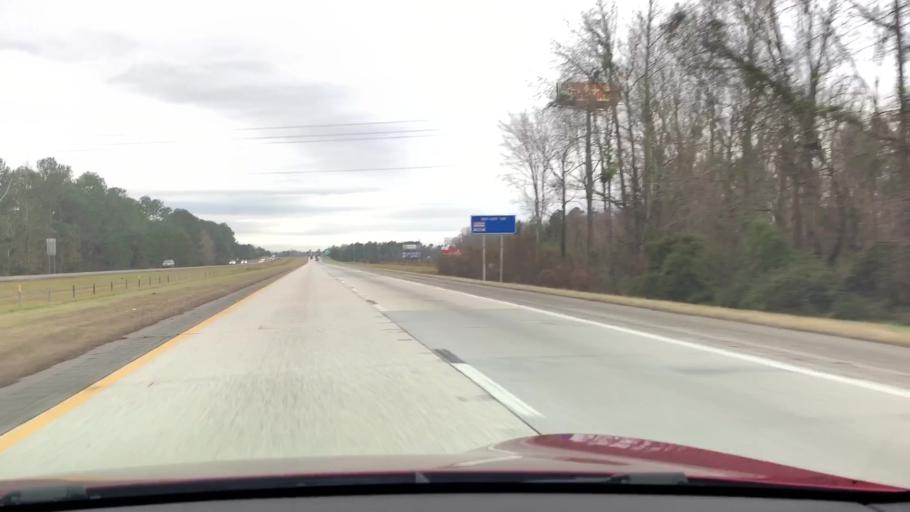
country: US
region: South Carolina
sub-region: Clarendon County
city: Manning
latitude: 33.7437
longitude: -80.2016
